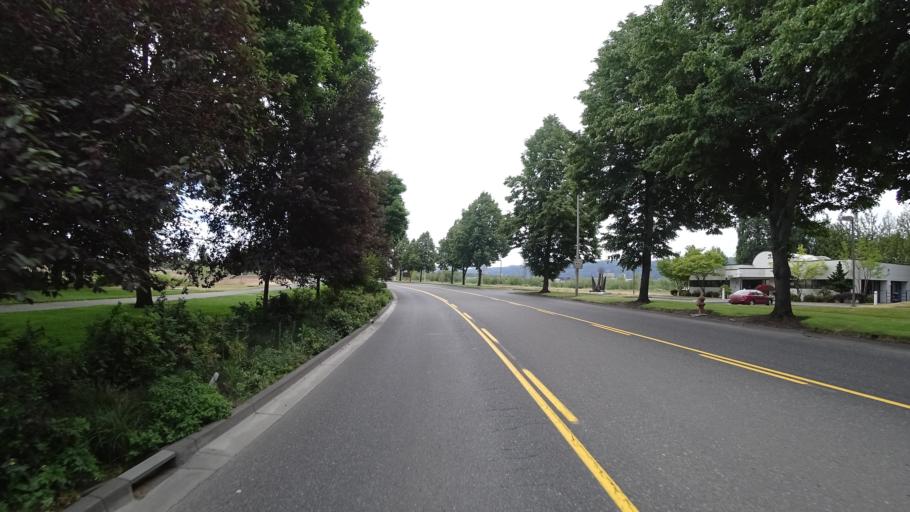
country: US
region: Oregon
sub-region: Washington County
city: West Haven
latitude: 45.6189
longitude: -122.7713
